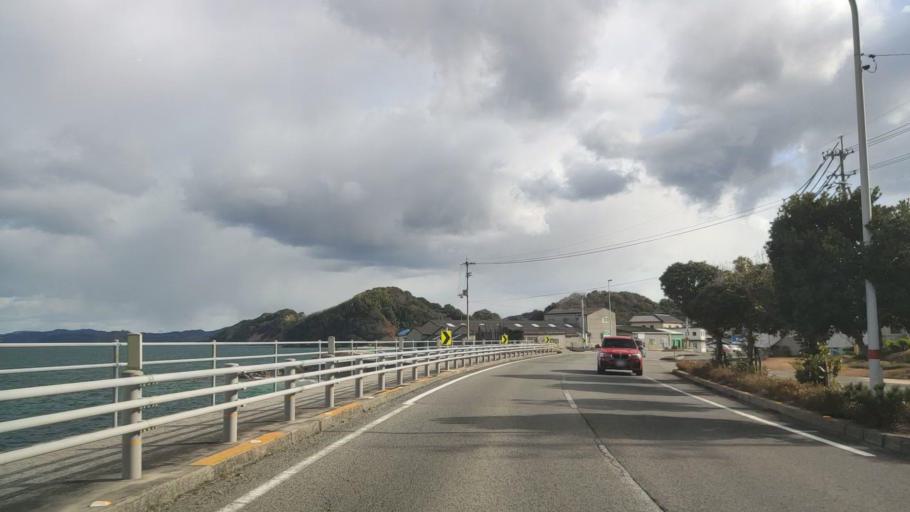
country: JP
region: Ehime
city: Hojo
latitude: 34.0587
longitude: 132.8822
